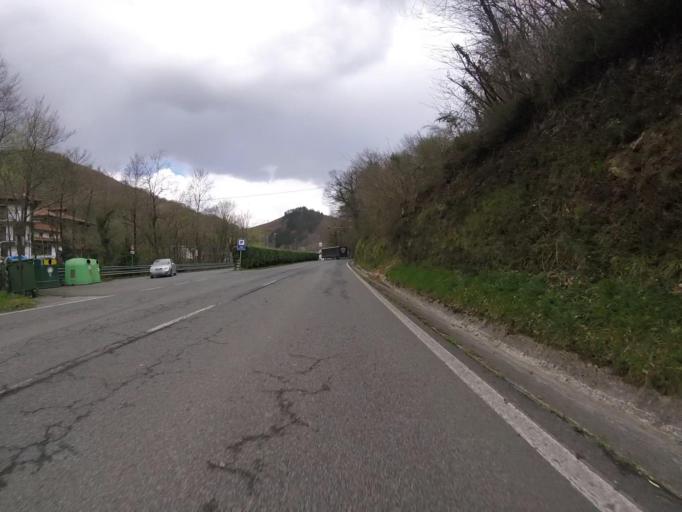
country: ES
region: Navarre
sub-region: Provincia de Navarra
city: Lesaka
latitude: 43.2418
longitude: -1.6697
